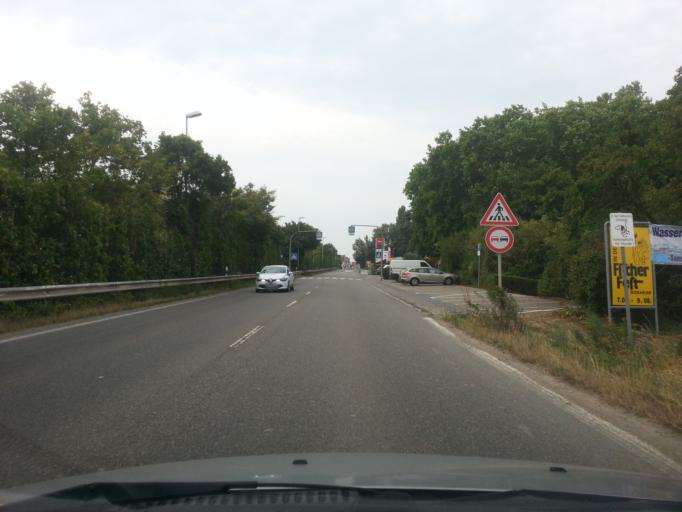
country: DE
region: Rheinland-Pfalz
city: Bobenheim-Roxheim
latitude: 49.5935
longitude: 8.3567
